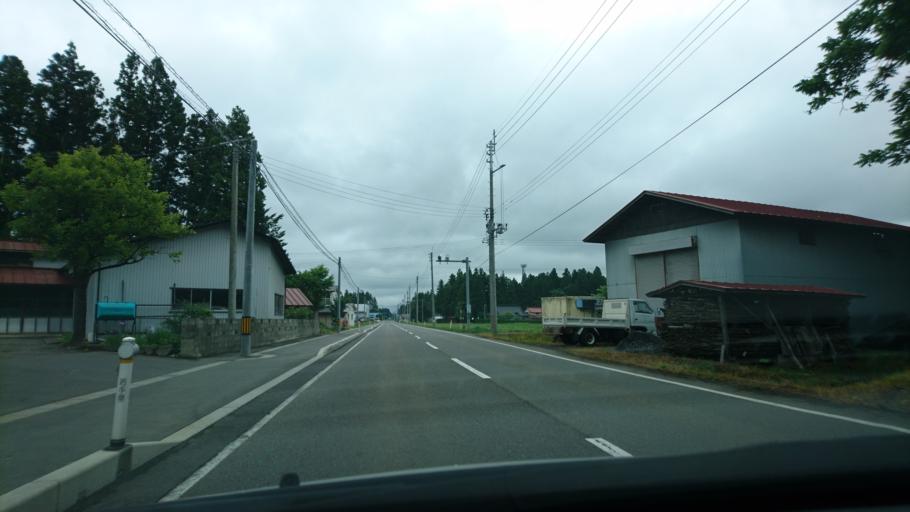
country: JP
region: Iwate
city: Mizusawa
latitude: 39.1040
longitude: 141.0517
